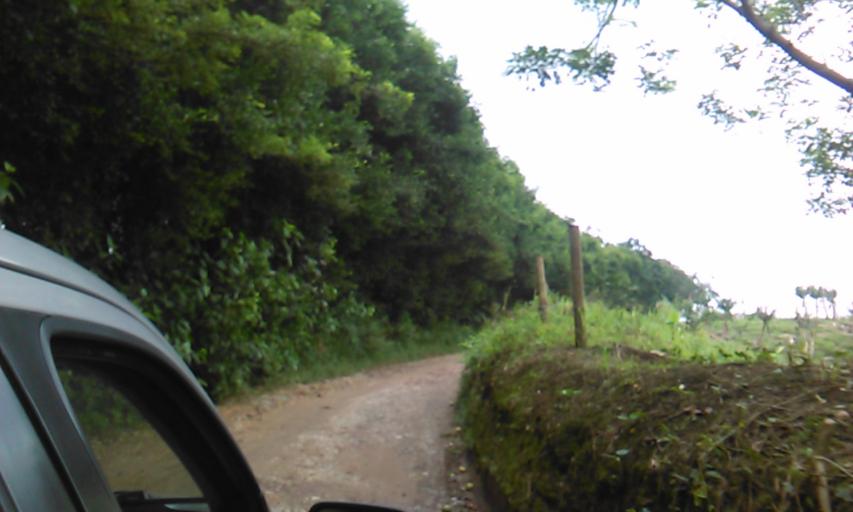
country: CO
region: Quindio
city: La Tebaida
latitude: 4.5086
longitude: -75.8580
